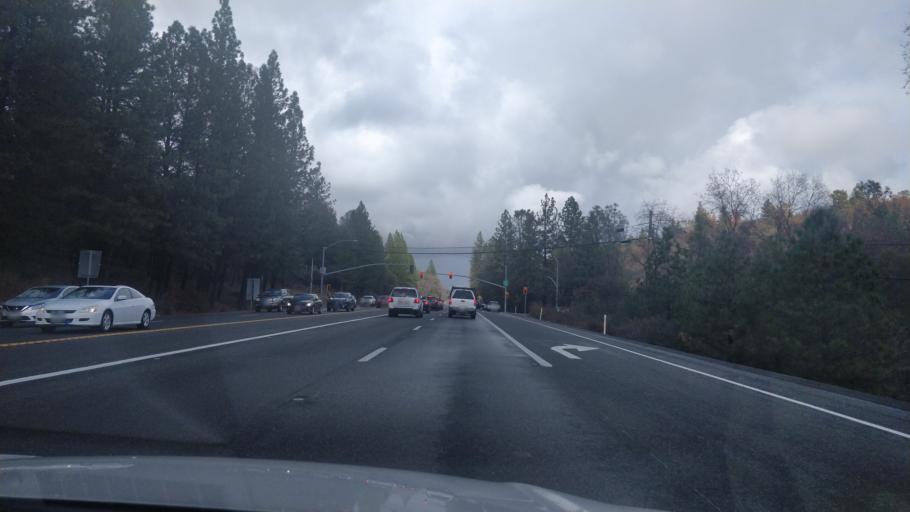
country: US
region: California
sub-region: Nevada County
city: Alta Sierra
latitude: 39.1119
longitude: -121.0828
